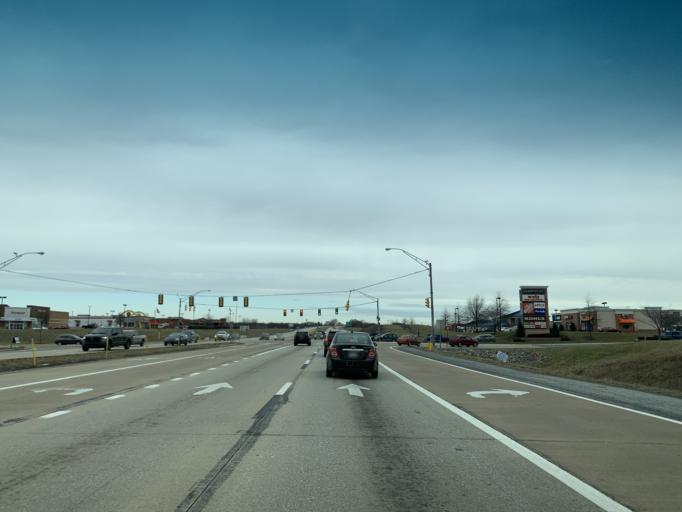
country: US
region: West Virginia
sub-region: Jefferson County
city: Ranson
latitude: 39.3190
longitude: -77.8491
